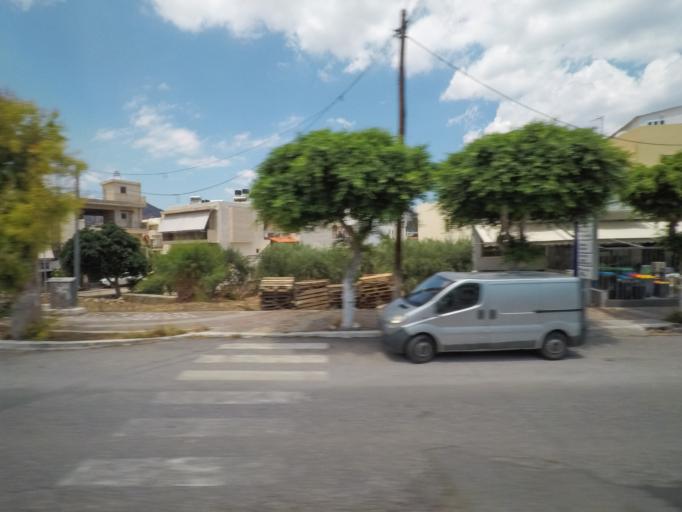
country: GR
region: Crete
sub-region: Nomos Lasithiou
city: Agios Nikolaos
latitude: 35.1864
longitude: 25.7089
